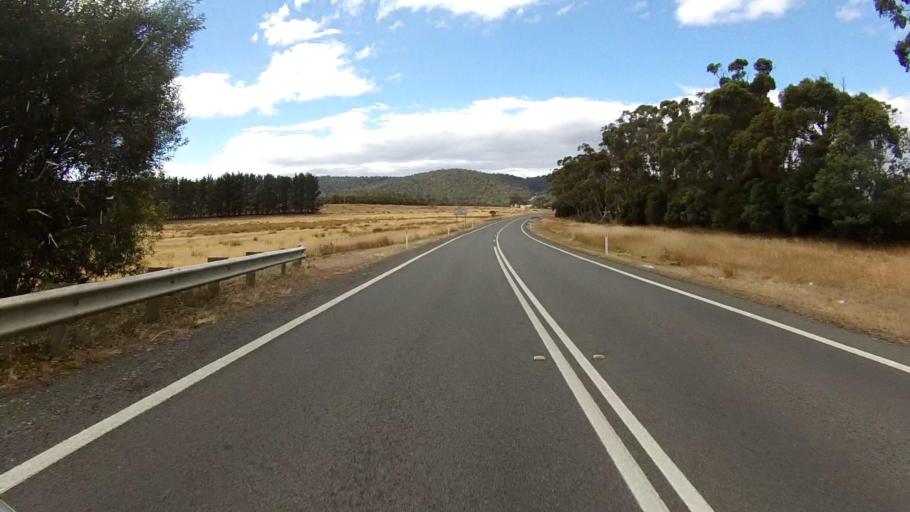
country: AU
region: Tasmania
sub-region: Sorell
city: Sorell
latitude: -42.6374
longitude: 147.5901
